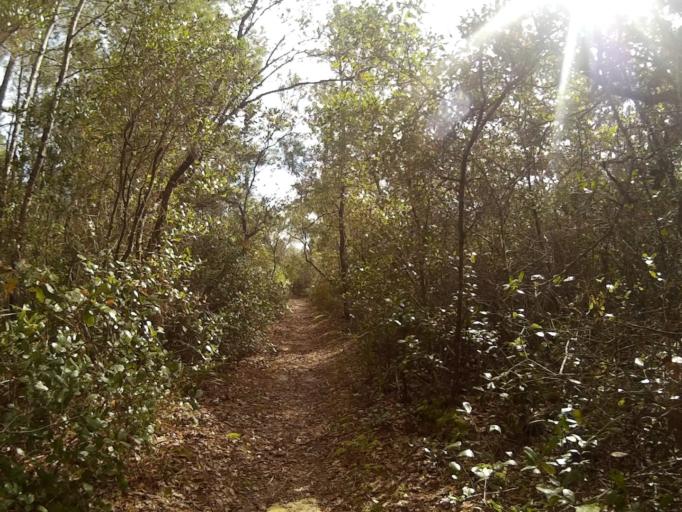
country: US
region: Florida
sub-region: Lake County
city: Astor
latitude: 29.0677
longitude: -81.6113
